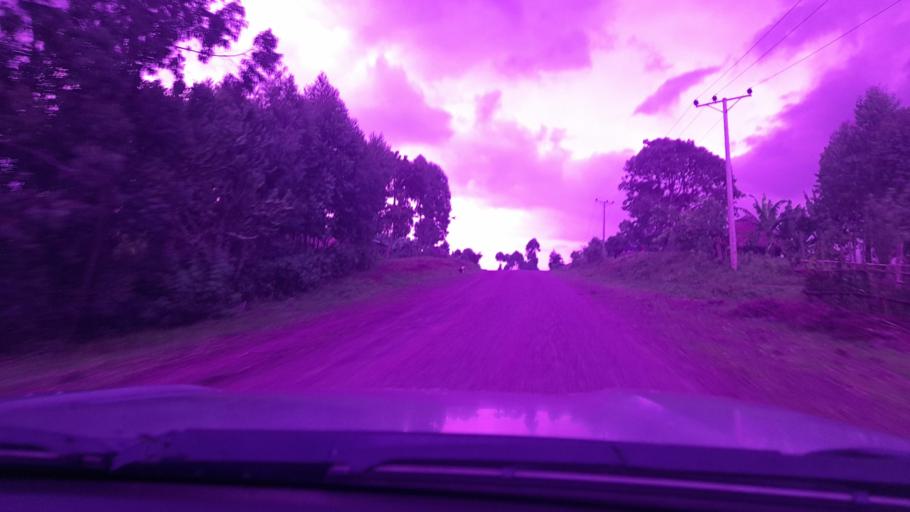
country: ET
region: Southern Nations, Nationalities, and People's Region
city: Mizan Teferi
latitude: 6.8982
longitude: 35.8431
